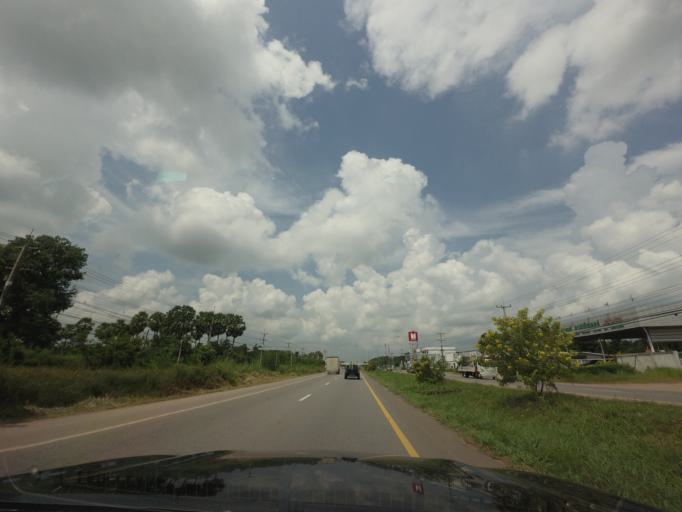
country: TH
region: Khon Kaen
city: Nong Ruea
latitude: 16.4900
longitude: 102.4475
